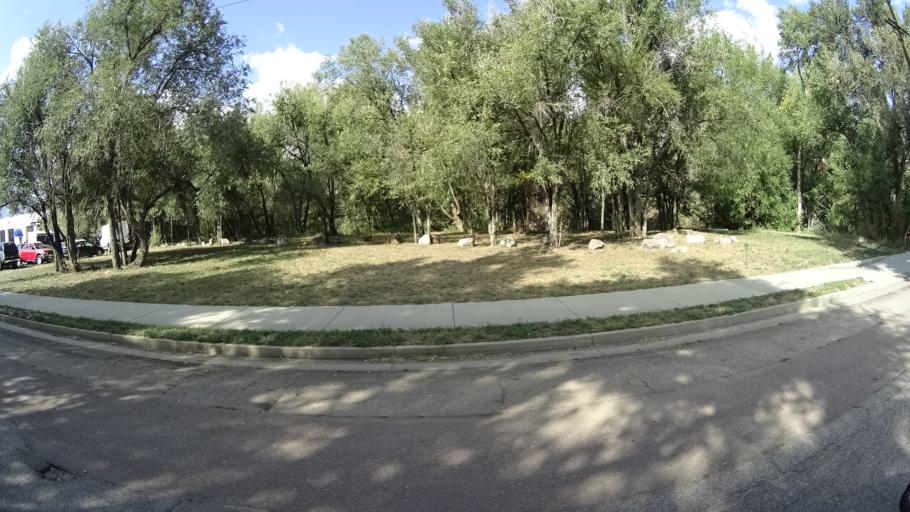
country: US
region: Colorado
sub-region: El Paso County
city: Colorado Springs
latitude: 38.8318
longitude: -104.8131
